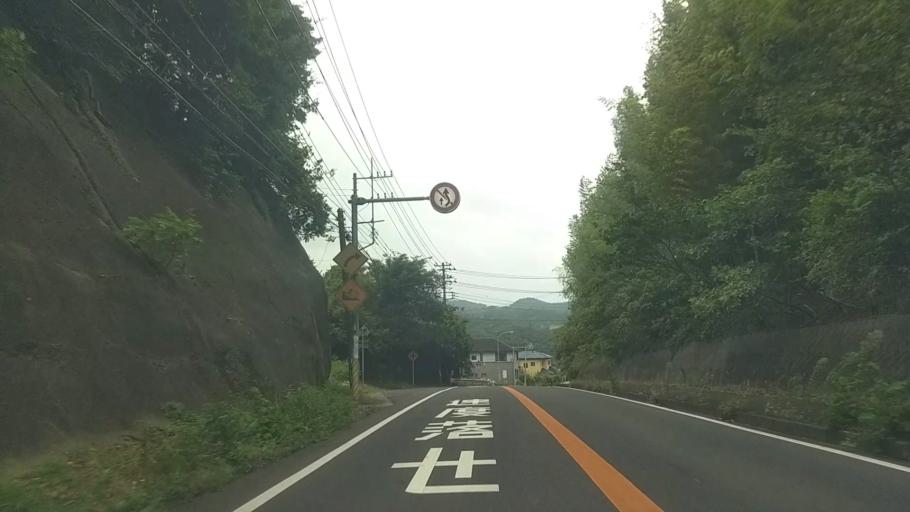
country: JP
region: Chiba
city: Kisarazu
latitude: 35.2834
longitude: 140.0804
